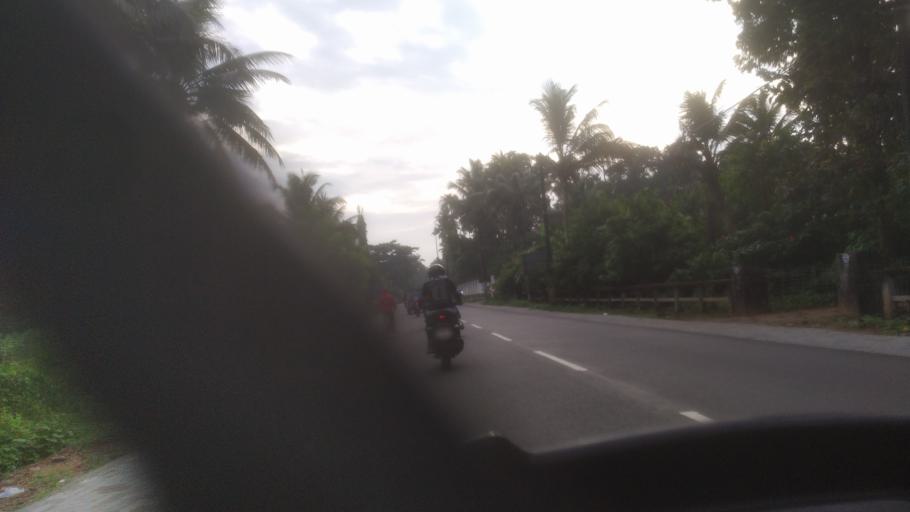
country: IN
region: Kerala
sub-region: Ernakulam
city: Kotamangalam
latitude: 10.0599
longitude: 76.6364
